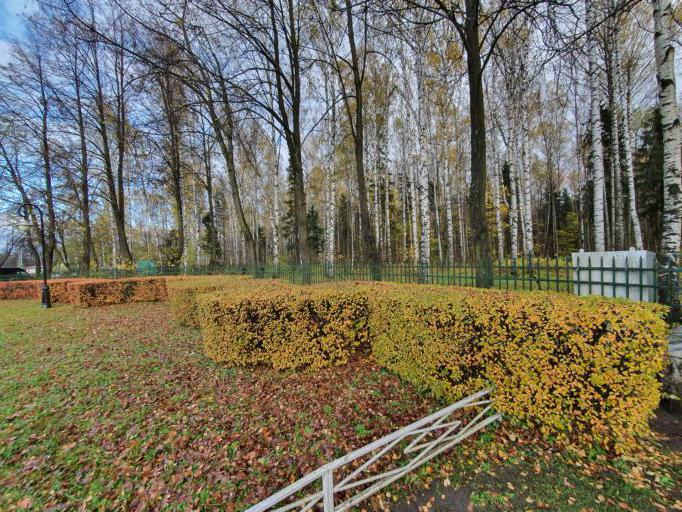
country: RU
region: St.-Petersburg
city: Pavlovsk
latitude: 59.6930
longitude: 30.4345
